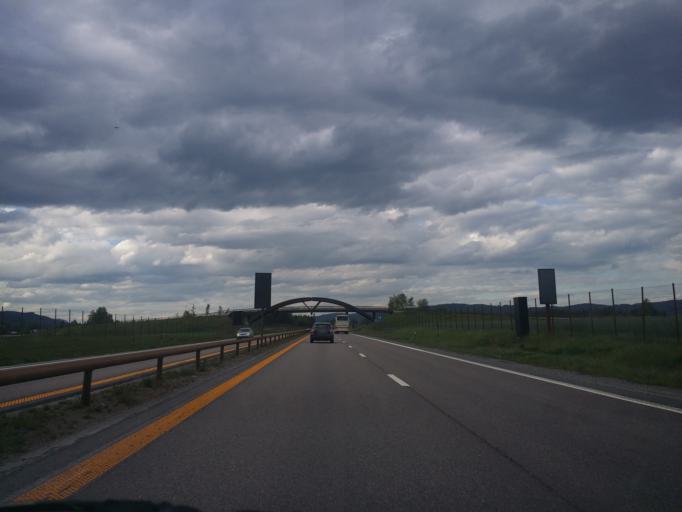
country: NO
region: Akershus
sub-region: Eidsvoll
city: Eidsvoll
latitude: 60.3790
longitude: 11.2091
